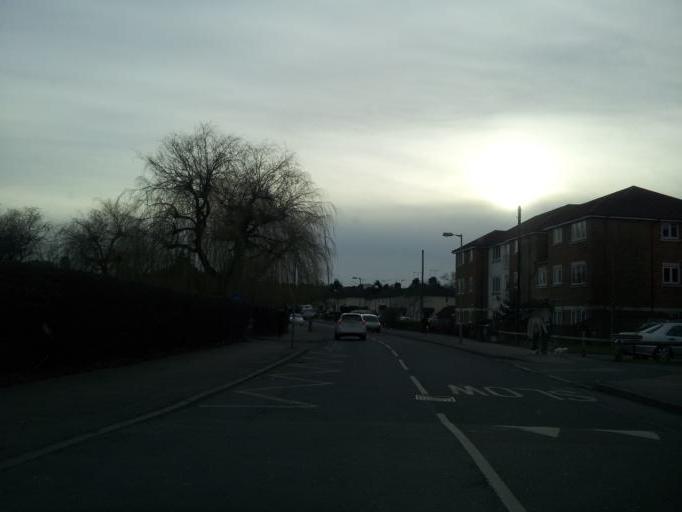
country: GB
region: England
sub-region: Hertfordshire
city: Bushey
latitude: 51.6479
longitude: -0.3561
